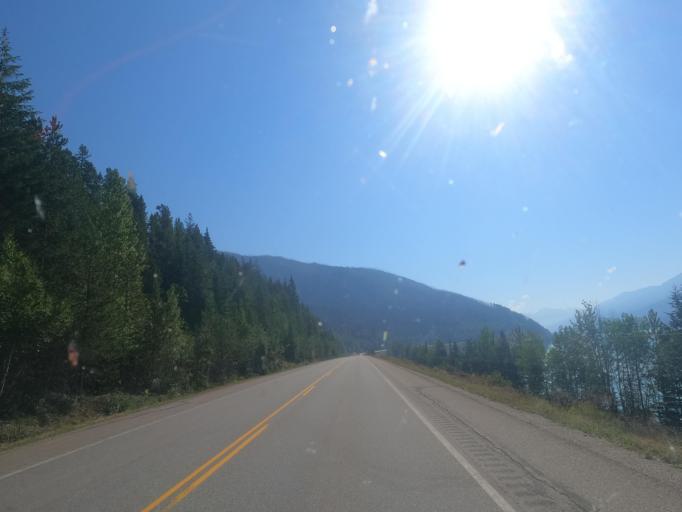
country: CA
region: Alberta
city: Jasper Park Lodge
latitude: 52.9539
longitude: -118.8793
